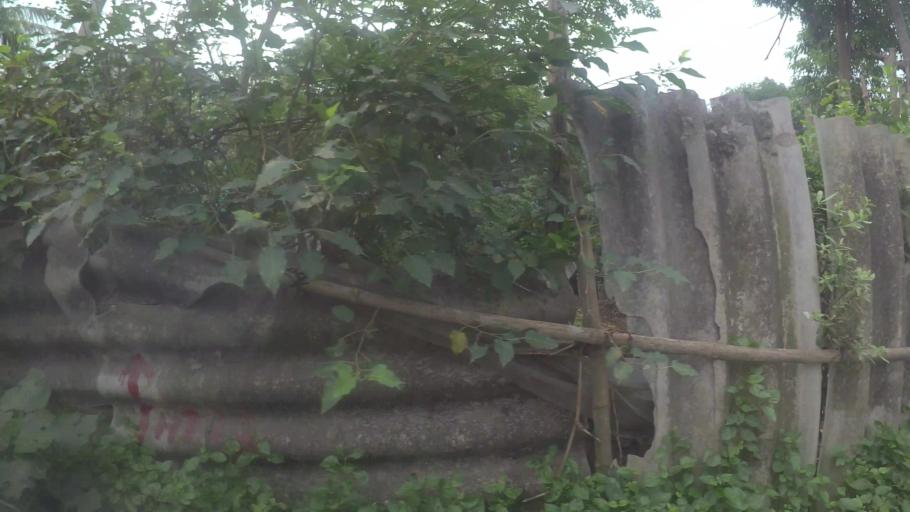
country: VN
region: Ha Noi
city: Ha Dong
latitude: 20.9709
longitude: 105.7641
